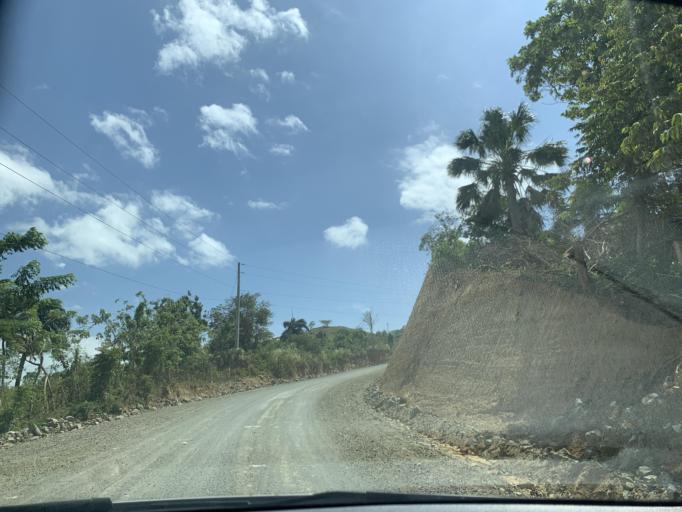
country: DO
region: Puerto Plata
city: Luperon
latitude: 19.8810
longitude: -70.8513
